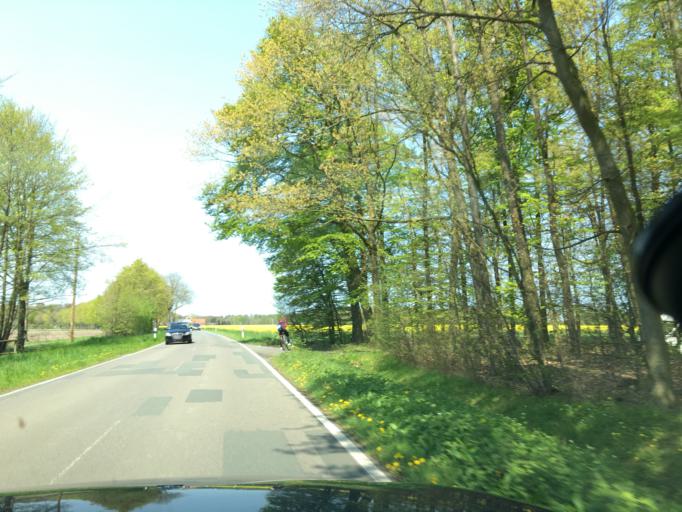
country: DE
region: North Rhine-Westphalia
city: Ludinghausen
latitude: 51.7816
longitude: 7.4368
